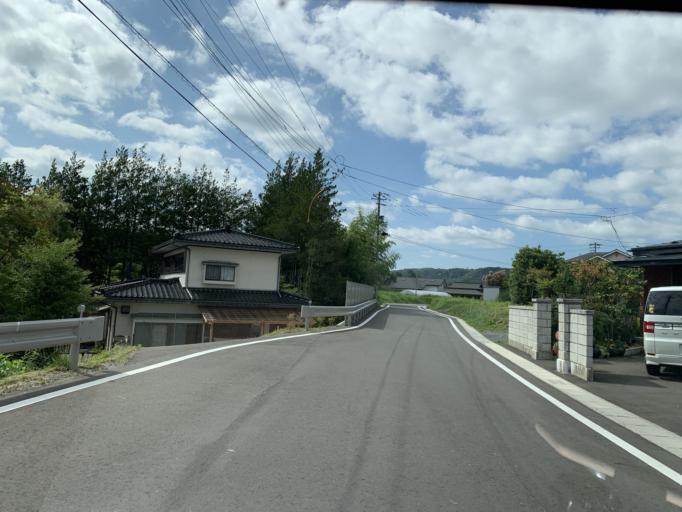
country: JP
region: Iwate
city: Ichinoseki
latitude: 38.9293
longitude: 141.0950
